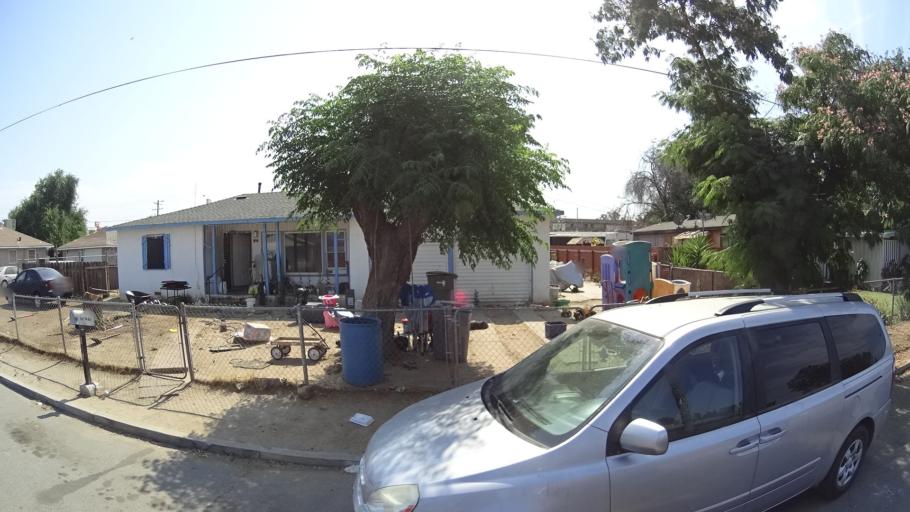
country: US
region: California
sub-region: Fresno County
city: West Park
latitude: 36.7541
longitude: -119.8307
